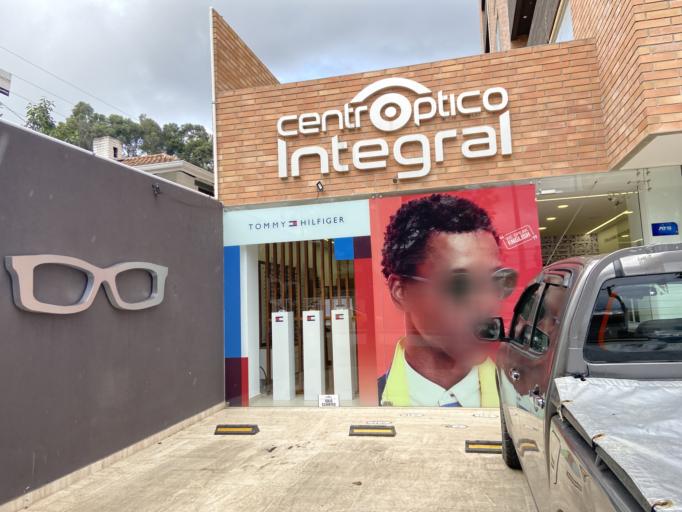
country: EC
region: Azuay
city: Cuenca
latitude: -2.8908
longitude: -79.0255
